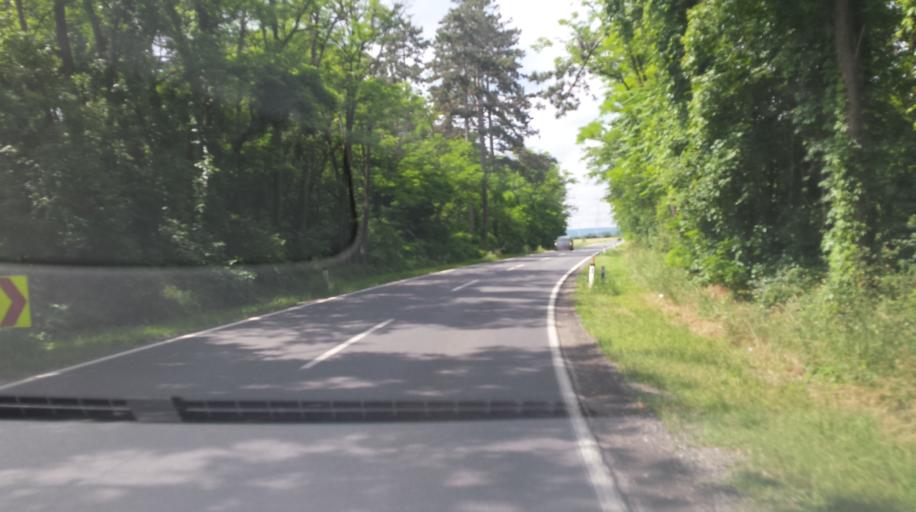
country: AT
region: Lower Austria
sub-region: Politischer Bezirk Ganserndorf
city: Aderklaa
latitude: 48.3053
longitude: 16.5409
